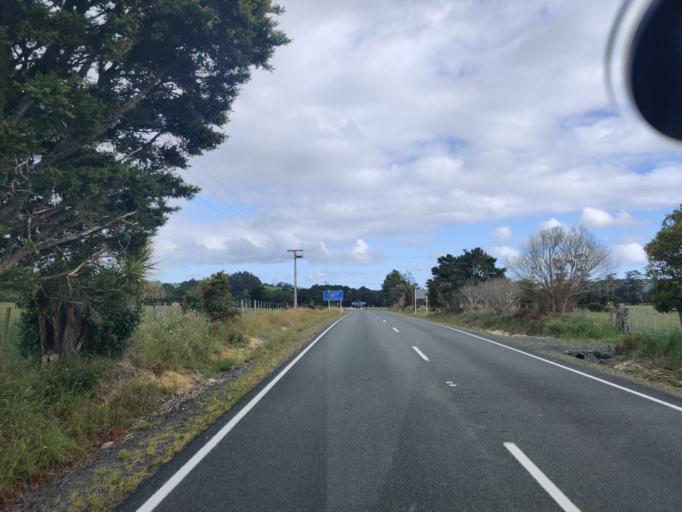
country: NZ
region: Northland
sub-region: Whangarei
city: Ngunguru
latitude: -35.5645
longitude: 174.3921
